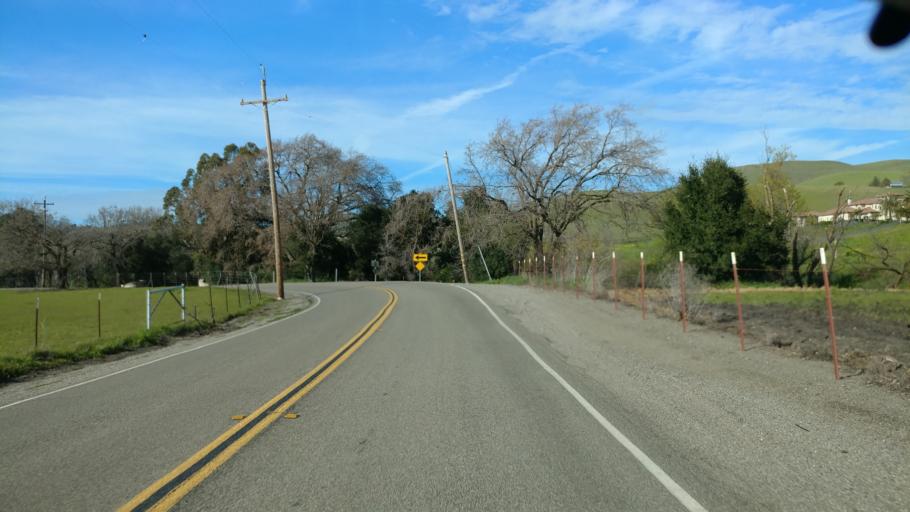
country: US
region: California
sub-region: Alameda County
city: Livermore
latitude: 37.7590
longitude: -121.7791
